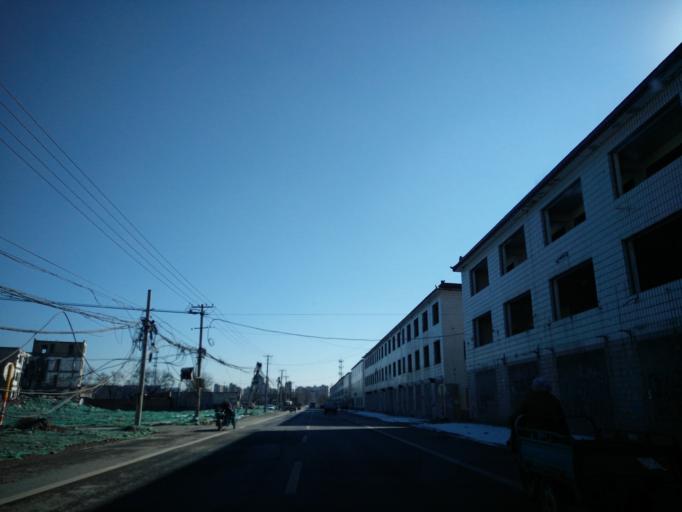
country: CN
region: Beijing
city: Yinghai
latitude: 39.7533
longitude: 116.4623
